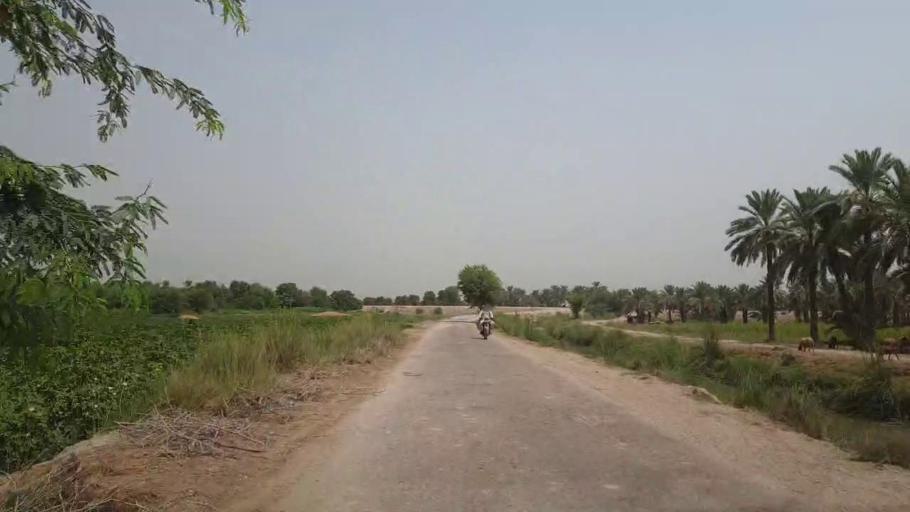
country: PK
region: Sindh
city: Gambat
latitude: 27.4355
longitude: 68.5597
